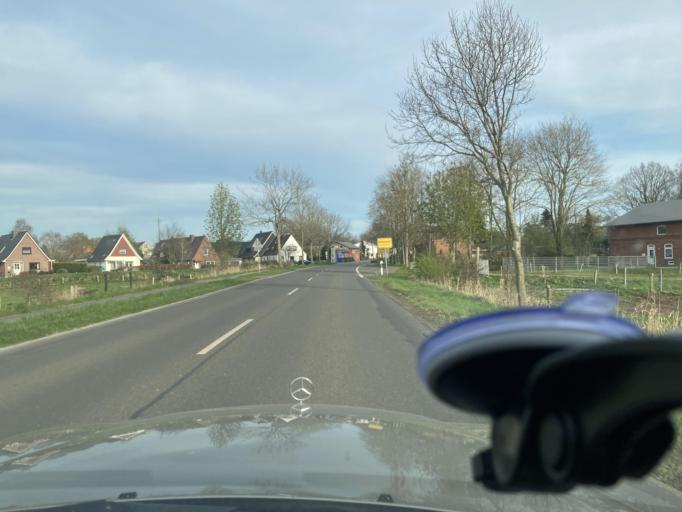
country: DE
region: Schleswig-Holstein
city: Weddingstedt
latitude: 54.2402
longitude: 9.0827
